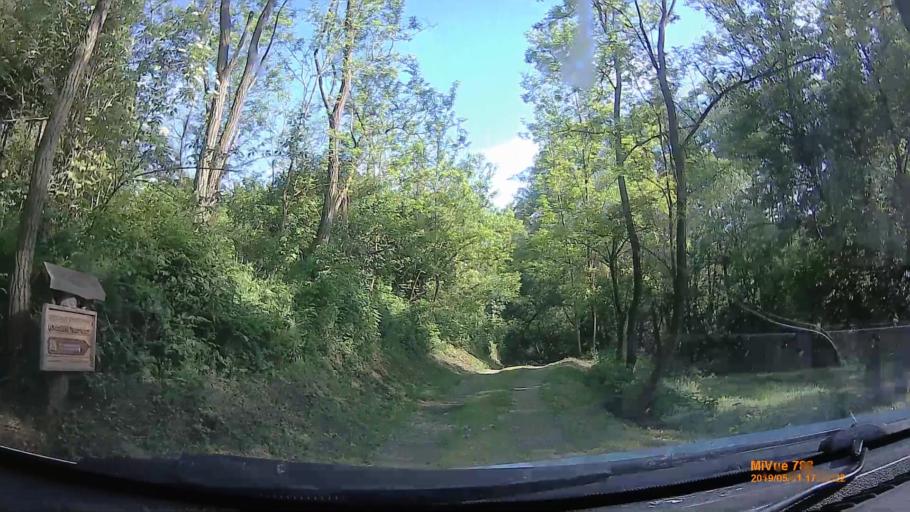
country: HU
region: Nograd
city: Nagyoroszi
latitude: 48.0294
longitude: 19.0461
